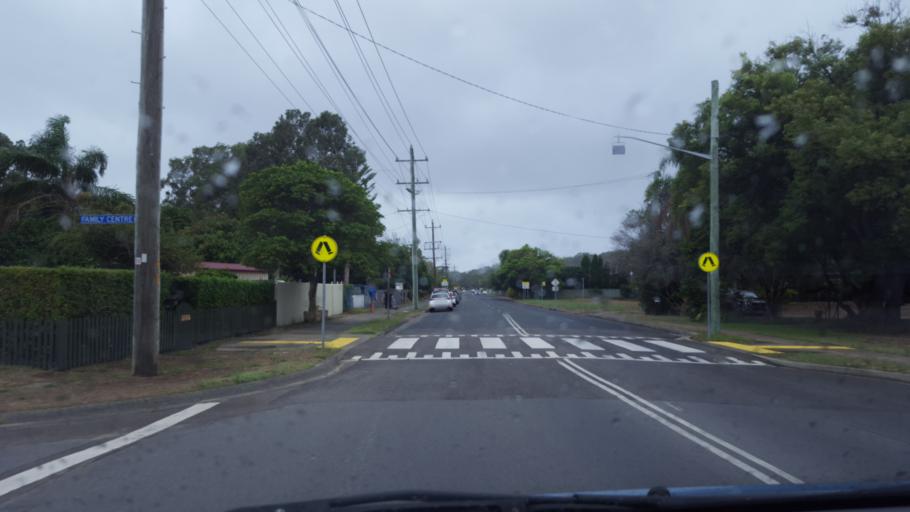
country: AU
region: New South Wales
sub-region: Port Stephens Shire
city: Anna Bay
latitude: -32.7774
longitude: 152.0863
